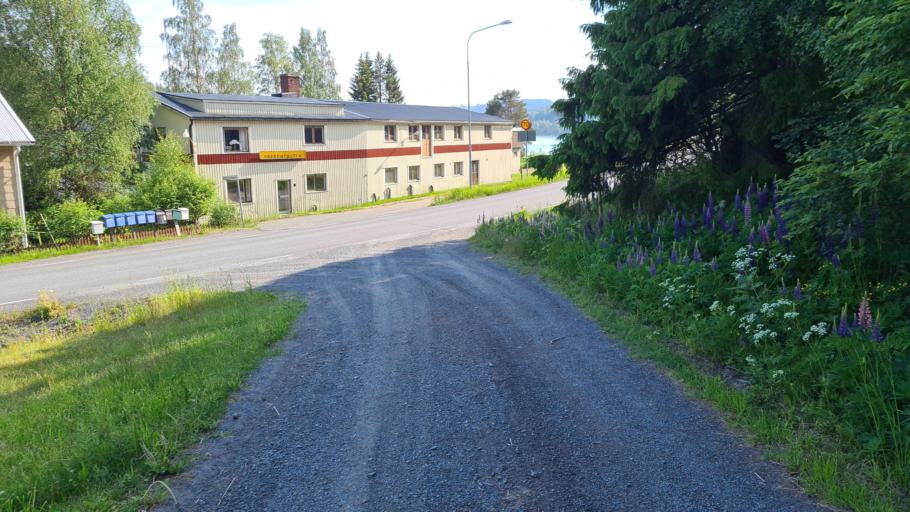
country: SE
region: Vaesternorrland
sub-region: Kramfors Kommun
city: Nordingra
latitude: 62.9827
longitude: 18.4185
